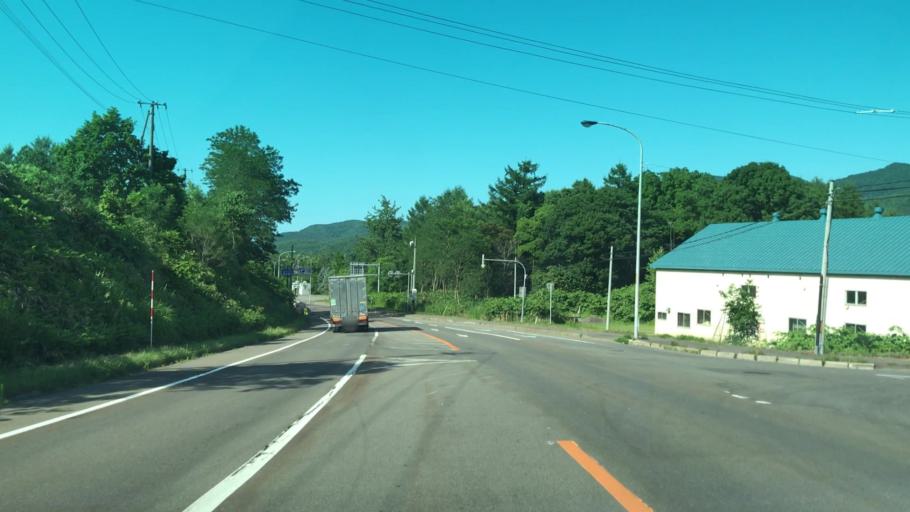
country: JP
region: Hokkaido
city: Yoichi
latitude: 43.0757
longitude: 140.7105
